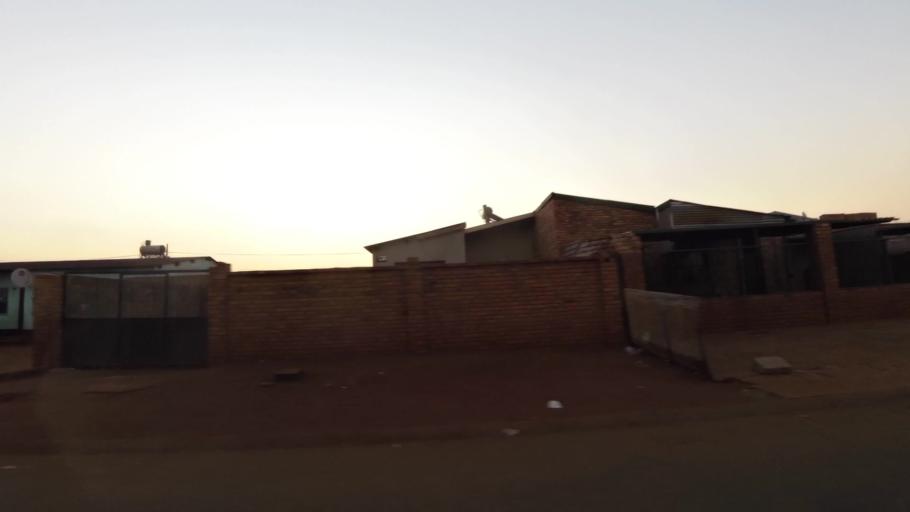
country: ZA
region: Gauteng
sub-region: City of Johannesburg Metropolitan Municipality
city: Soweto
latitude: -26.2908
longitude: 27.8733
